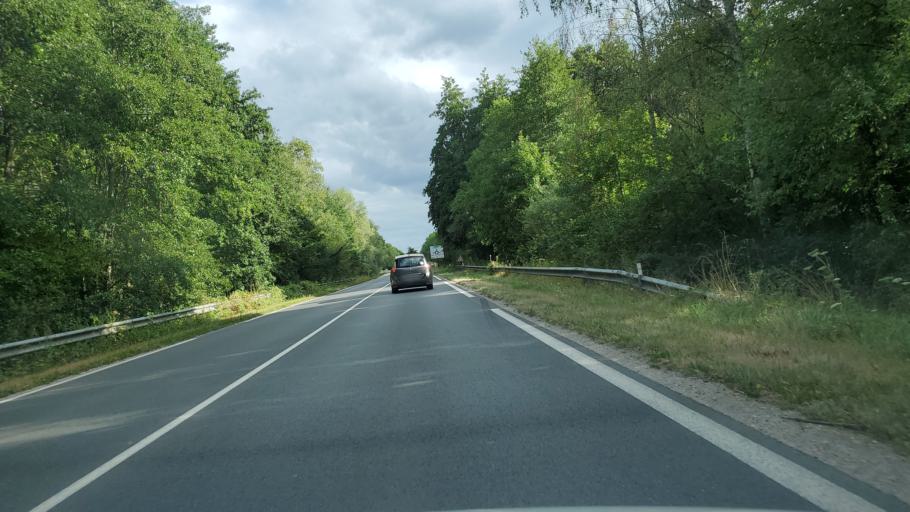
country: FR
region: Ile-de-France
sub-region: Departement de Seine-et-Marne
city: Villeneuve-le-Comte
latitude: 48.8179
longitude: 2.8420
